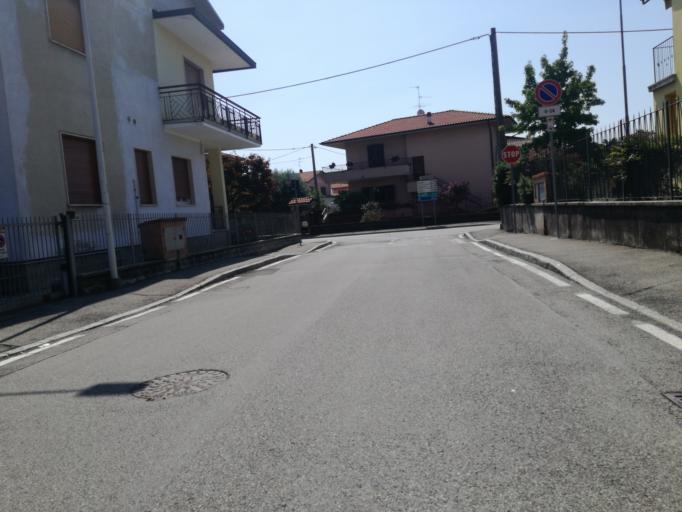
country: IT
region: Lombardy
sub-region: Provincia di Bergamo
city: Calusco d'Adda
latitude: 45.6870
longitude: 9.4805
